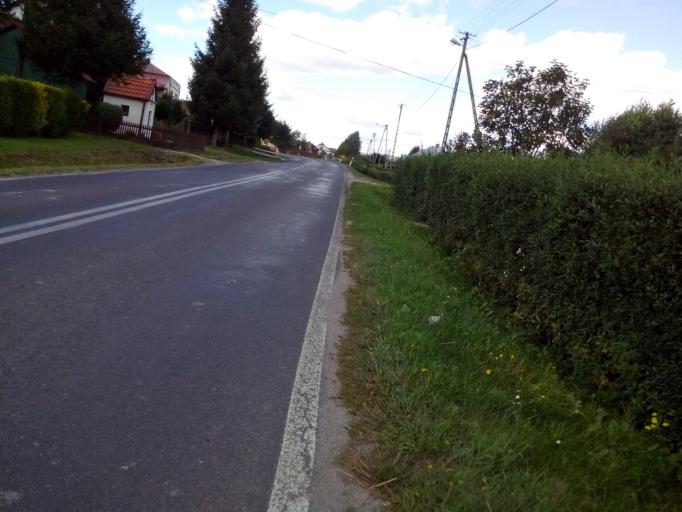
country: PL
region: Subcarpathian Voivodeship
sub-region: Powiat strzyzowski
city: Strzyzow
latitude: 49.8345
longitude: 21.8260
